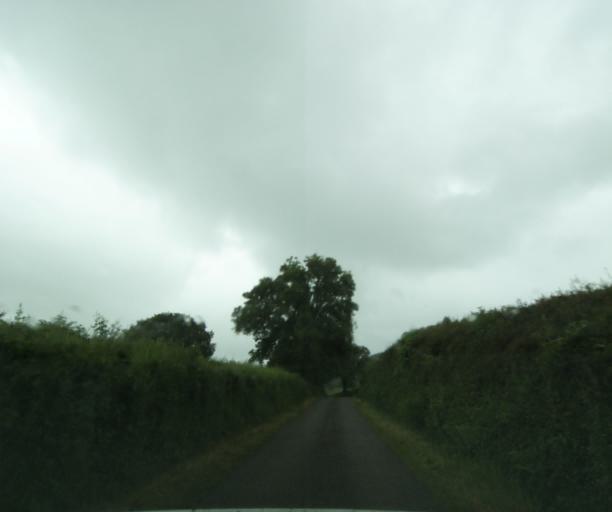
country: FR
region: Bourgogne
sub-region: Departement de Saone-et-Loire
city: Matour
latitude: 46.4194
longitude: 4.4762
